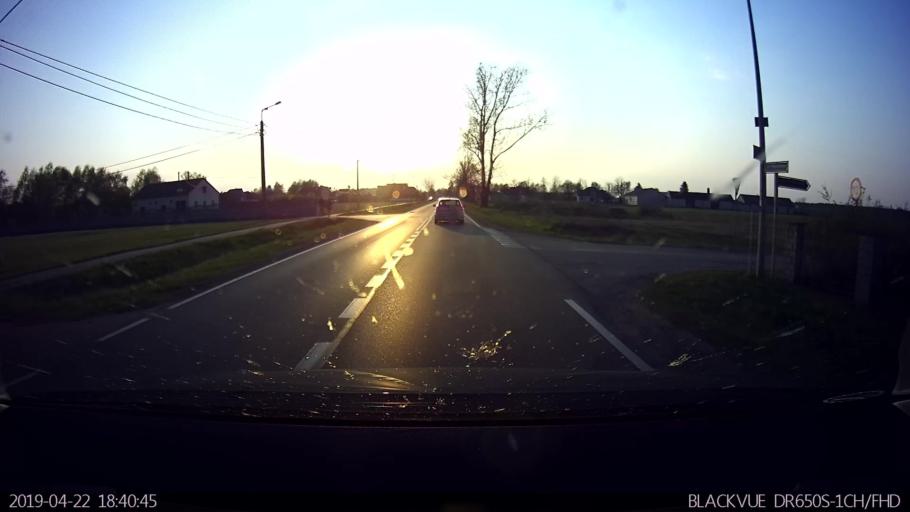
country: PL
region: Masovian Voivodeship
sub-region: Powiat wolominski
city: Dabrowka
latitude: 52.4469
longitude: 21.2729
